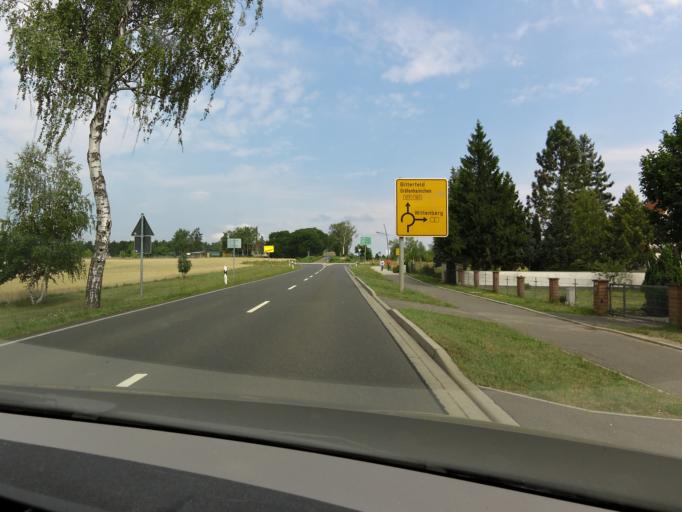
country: DE
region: Saxony
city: Bad Duben
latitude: 51.6032
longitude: 12.5744
